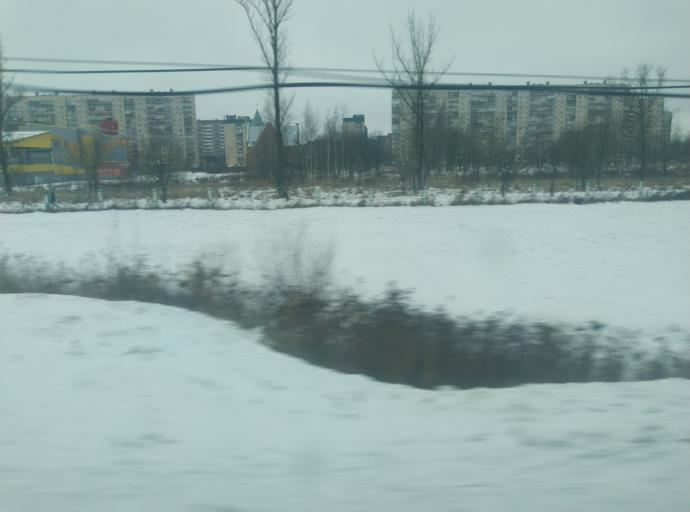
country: RU
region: St.-Petersburg
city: Kolpino
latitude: 59.7415
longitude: 30.6239
